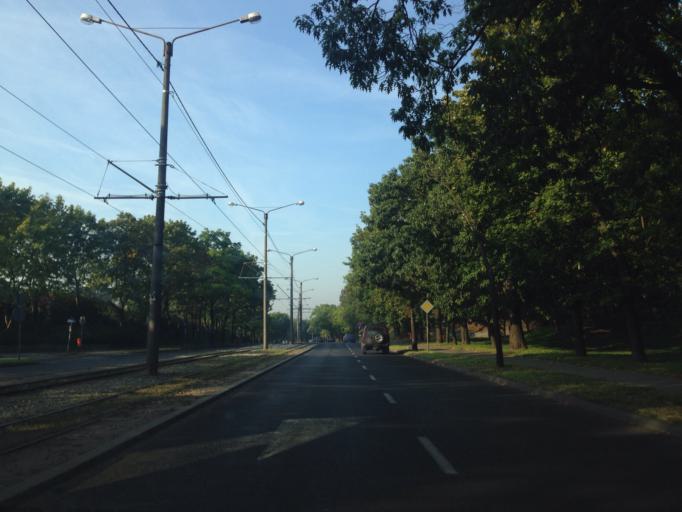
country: PL
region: Kujawsko-Pomorskie
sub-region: Torun
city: Torun
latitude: 53.0142
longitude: 18.6285
